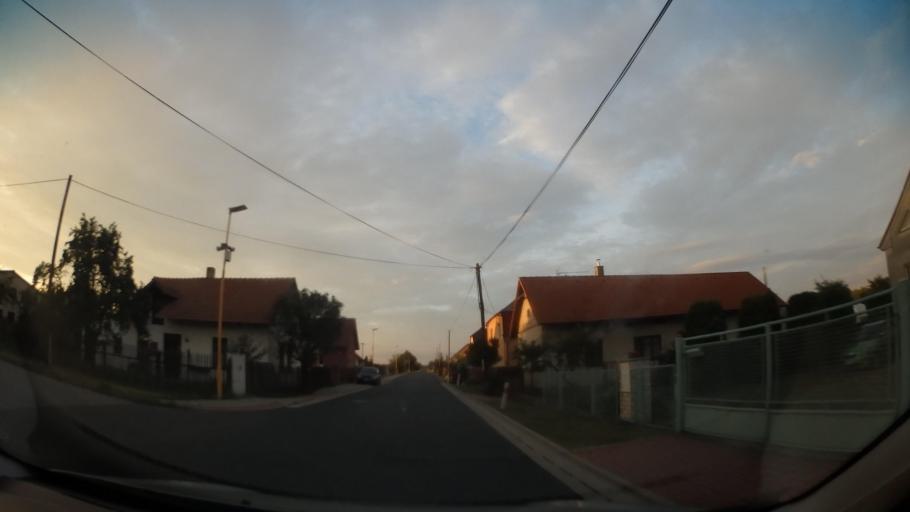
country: CZ
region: Central Bohemia
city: Loucen
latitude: 50.2435
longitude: 15.0230
